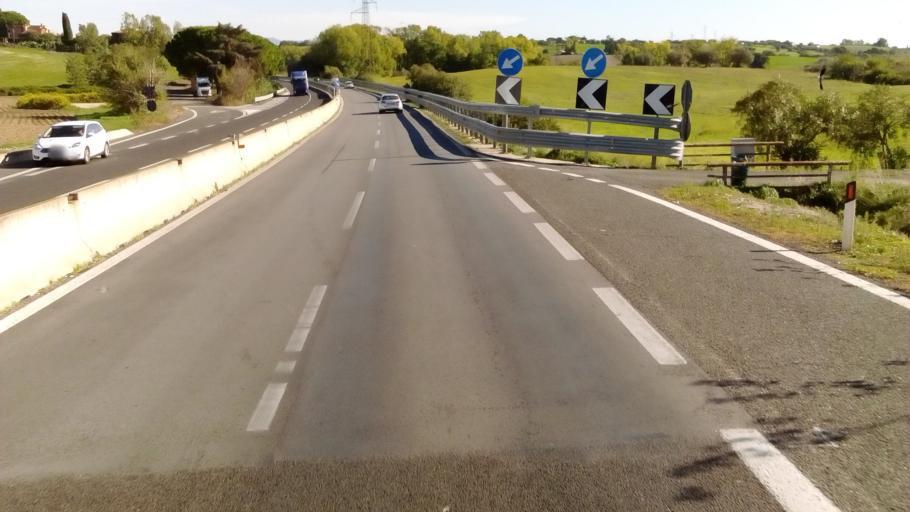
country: IT
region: Latium
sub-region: Provincia di Viterbo
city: Montalto di Castro
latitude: 42.3594
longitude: 11.5860
